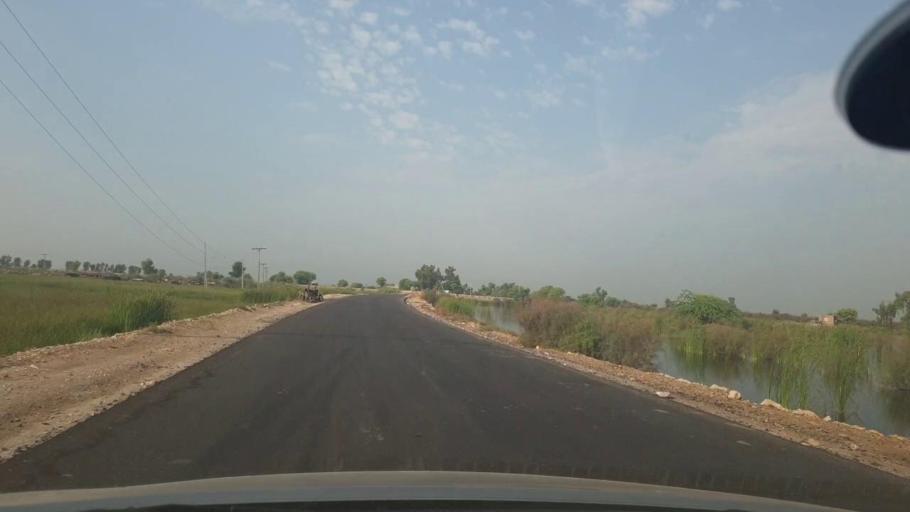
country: PK
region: Sindh
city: Jacobabad
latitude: 28.0938
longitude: 68.3288
